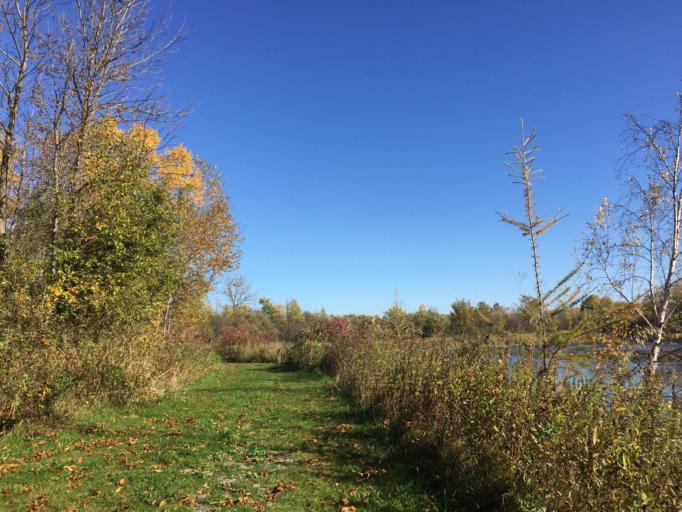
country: US
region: Minnesota
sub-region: Lake of the Woods County
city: Baudette
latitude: 48.2863
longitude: -94.5679
